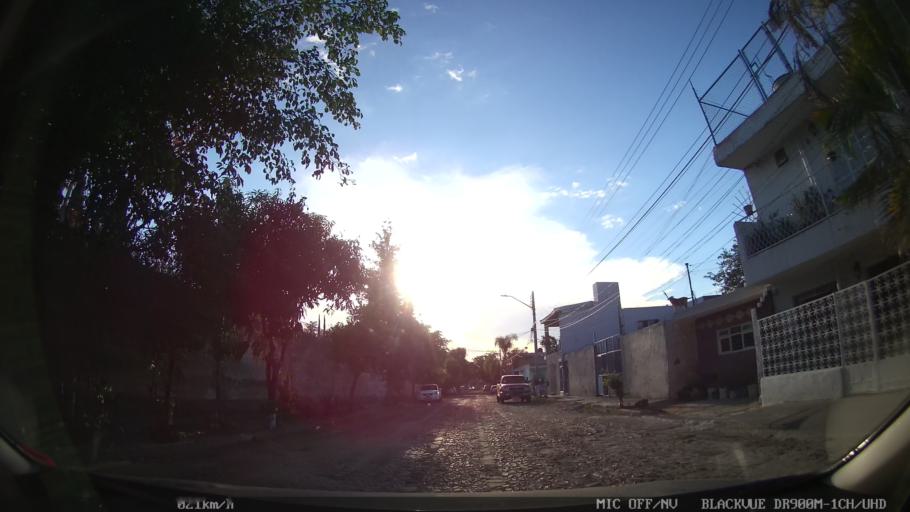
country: MX
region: Jalisco
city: Tlaquepaque
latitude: 20.7055
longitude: -103.2984
